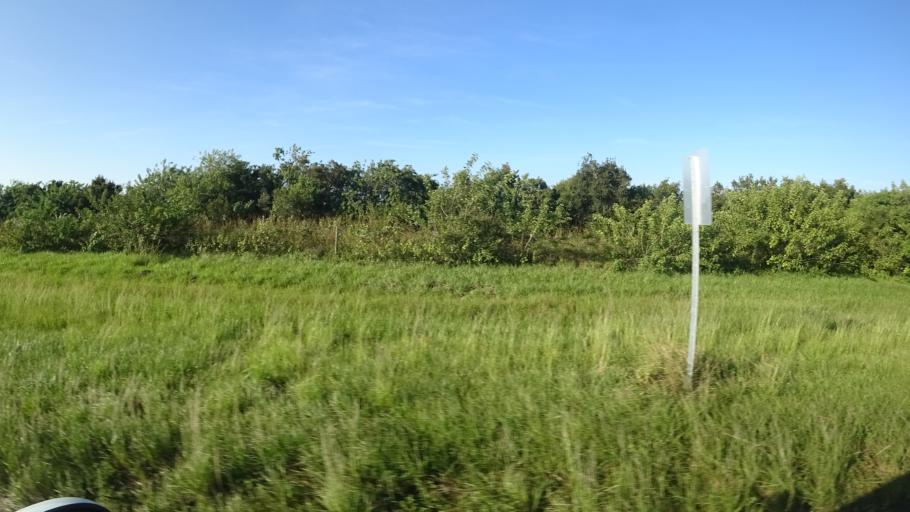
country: US
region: Florida
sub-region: Hillsborough County
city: Sun City Center
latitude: 27.5468
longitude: -82.3556
